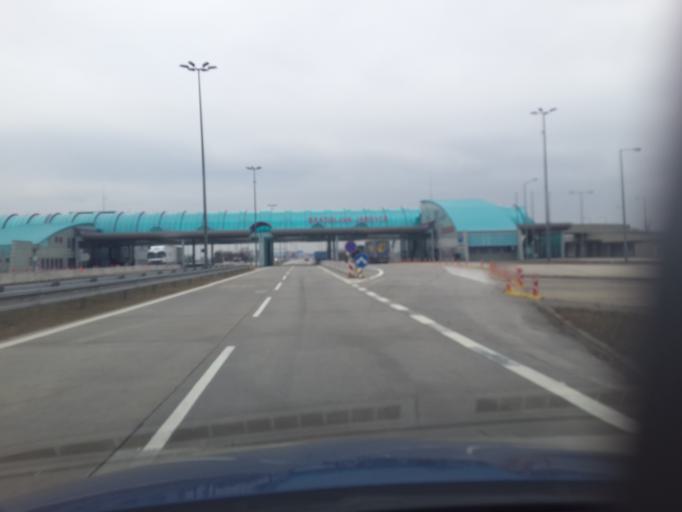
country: AT
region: Burgenland
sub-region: Politischer Bezirk Neusiedl am See
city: Kittsee
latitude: 48.0698
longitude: 17.0777
